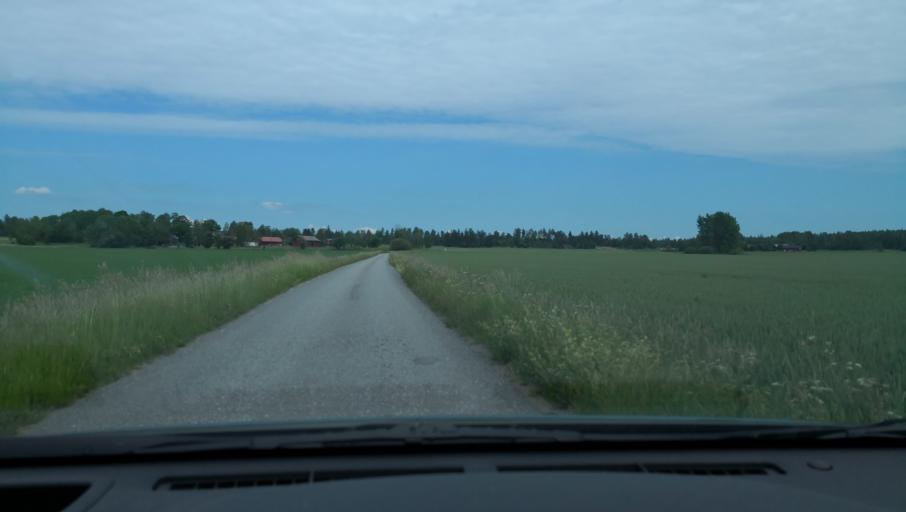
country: SE
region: Uppsala
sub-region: Enkopings Kommun
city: Orsundsbro
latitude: 59.6996
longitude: 17.4106
